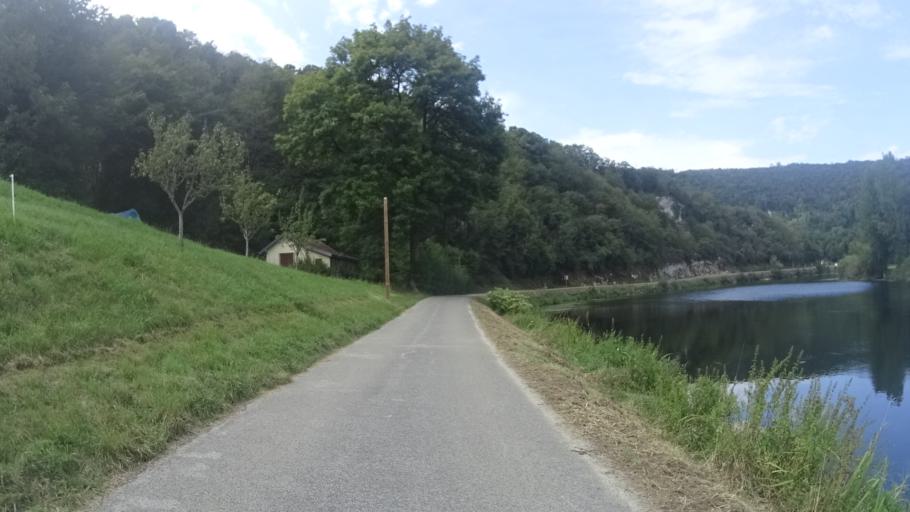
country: FR
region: Franche-Comte
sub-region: Departement du Doubs
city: Baume-les-Dames
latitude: 47.3676
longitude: 6.4291
